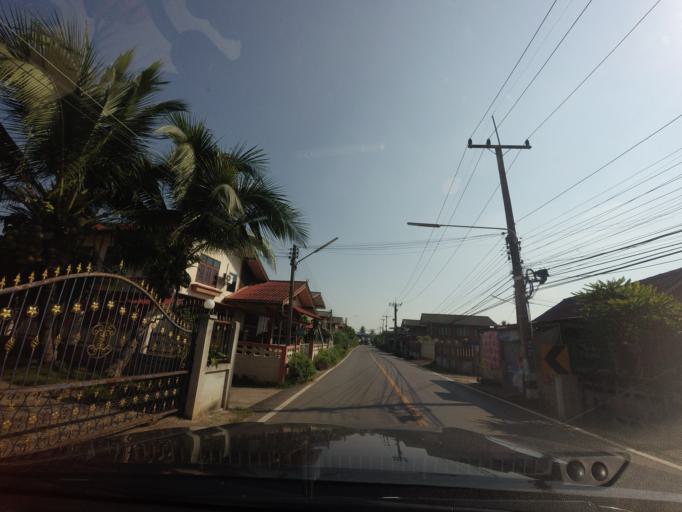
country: TH
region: Nan
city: Nan
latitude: 18.8563
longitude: 100.8111
